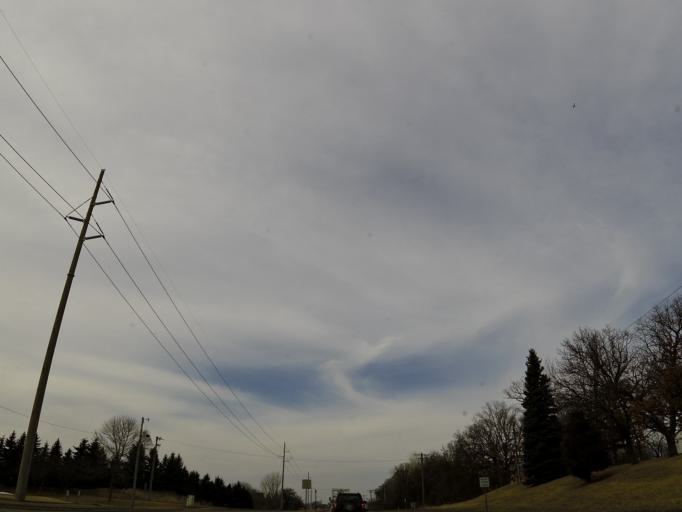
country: US
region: Minnesota
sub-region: Dakota County
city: Apple Valley
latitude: 44.7337
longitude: -93.2540
